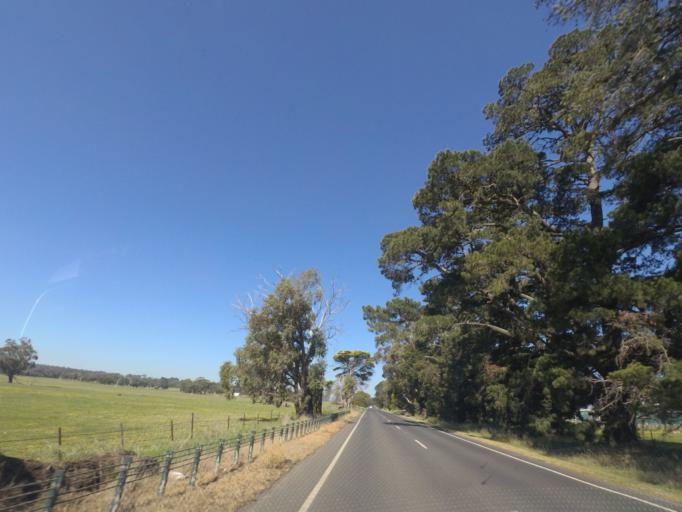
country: AU
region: Victoria
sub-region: Whittlesea
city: Whittlesea
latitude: -37.3267
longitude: 144.9713
